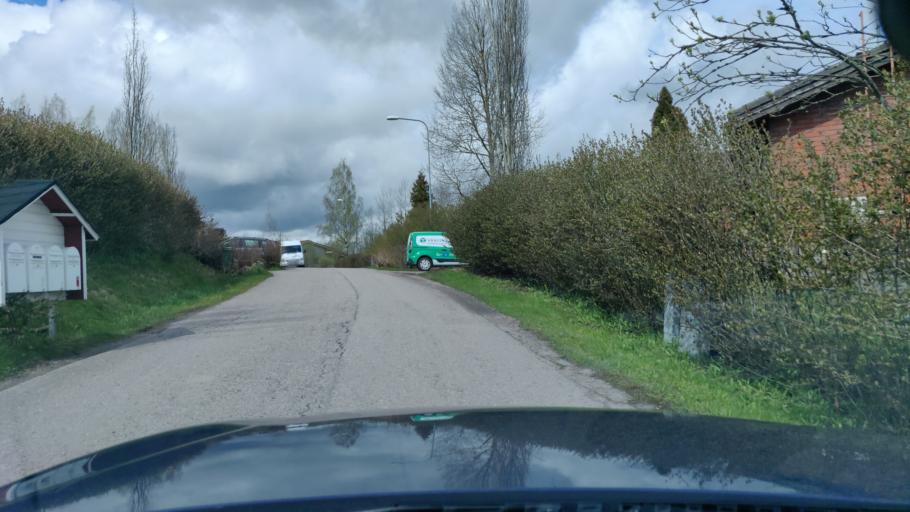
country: FI
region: Uusimaa
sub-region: Helsinki
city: Nurmijaervi
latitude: 60.3638
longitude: 24.7363
